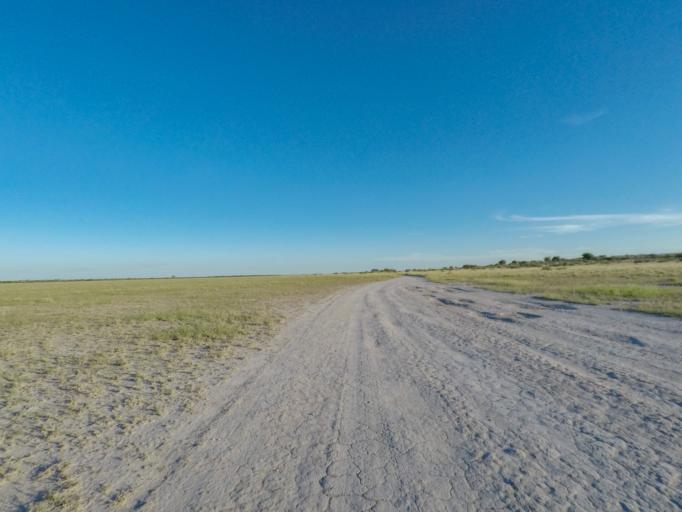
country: BW
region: Central
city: Rakops
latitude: -21.4011
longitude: 23.7953
